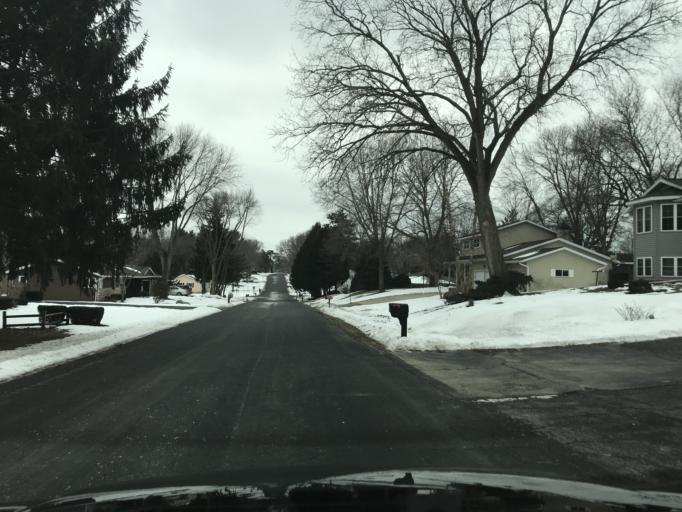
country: US
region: Wisconsin
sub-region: Dane County
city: Monona
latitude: 43.0829
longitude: -89.2710
